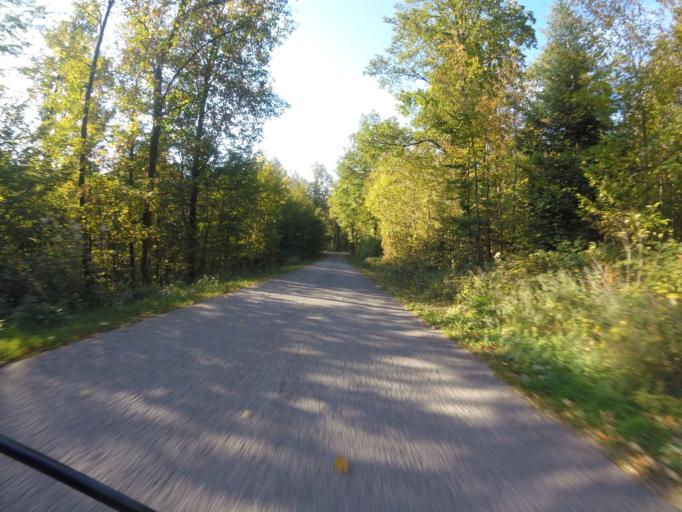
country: DE
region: Baden-Wuerttemberg
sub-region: Regierungsbezirk Stuttgart
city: Spiegelberg
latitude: 49.0069
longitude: 9.4303
